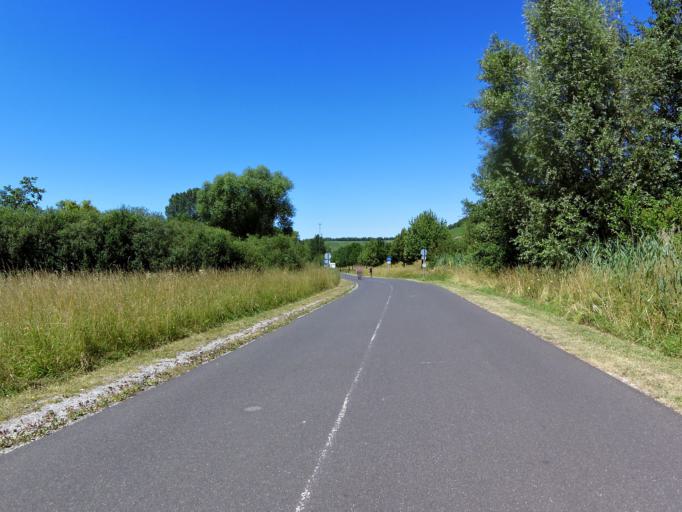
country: DE
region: Bavaria
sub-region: Regierungsbezirk Unterfranken
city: Randersacker
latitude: 49.7450
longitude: 9.9878
